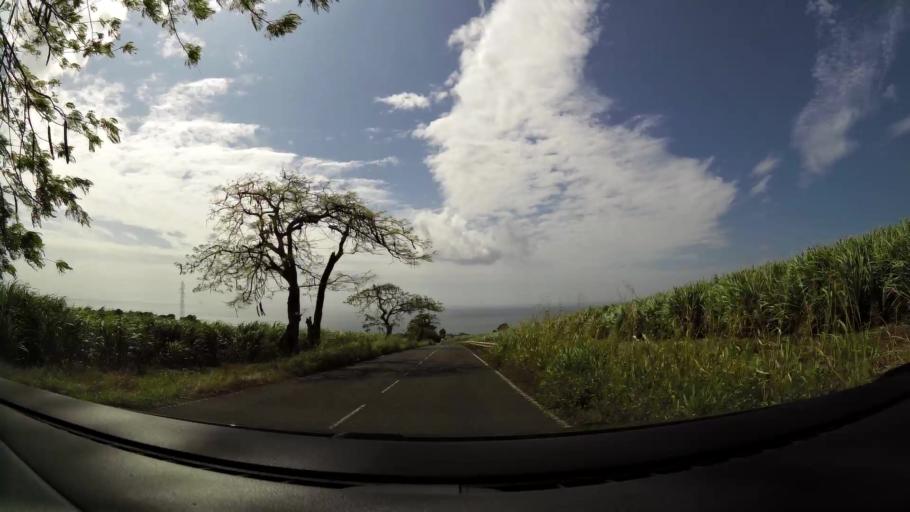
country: GP
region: Guadeloupe
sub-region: Guadeloupe
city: Basse-Terre
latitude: 16.0122
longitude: -61.7229
